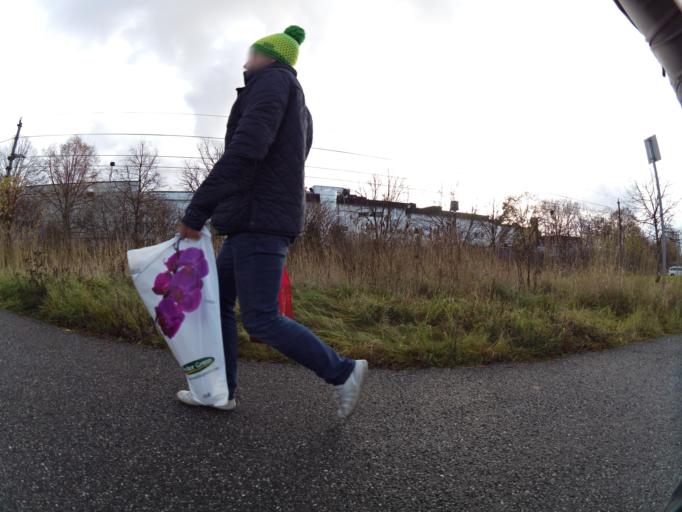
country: NO
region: Ostfold
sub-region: Sarpsborg
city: Sarpsborg
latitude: 59.2739
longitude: 11.0852
